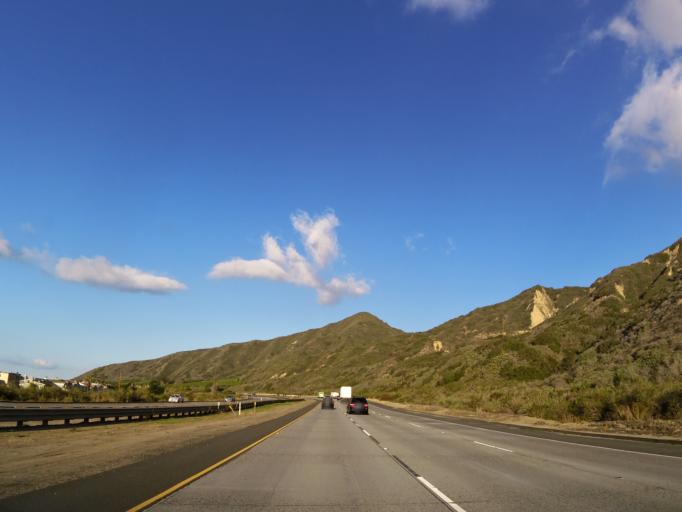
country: US
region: California
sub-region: Ventura County
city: Ventura
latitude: 34.3203
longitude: -119.3690
